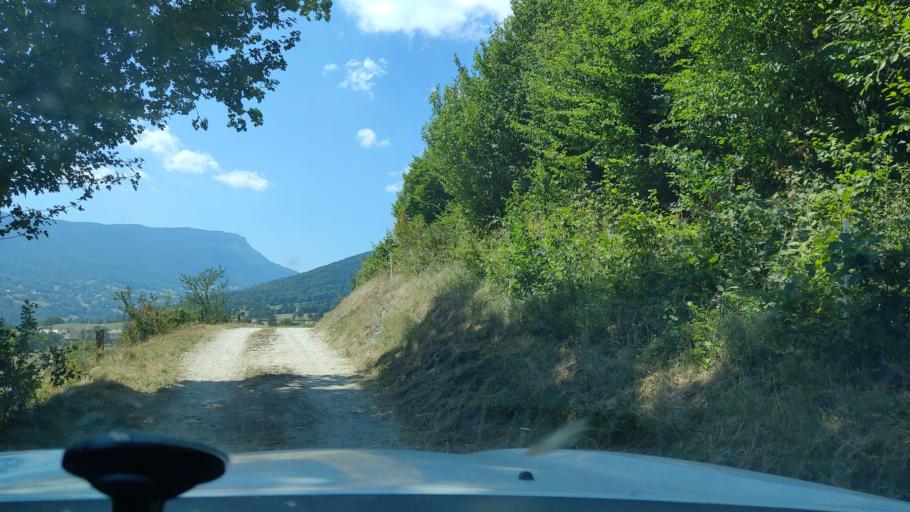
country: FR
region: Rhone-Alpes
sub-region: Departement de la Haute-Savoie
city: Gruffy
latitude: 45.7248
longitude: 6.0852
